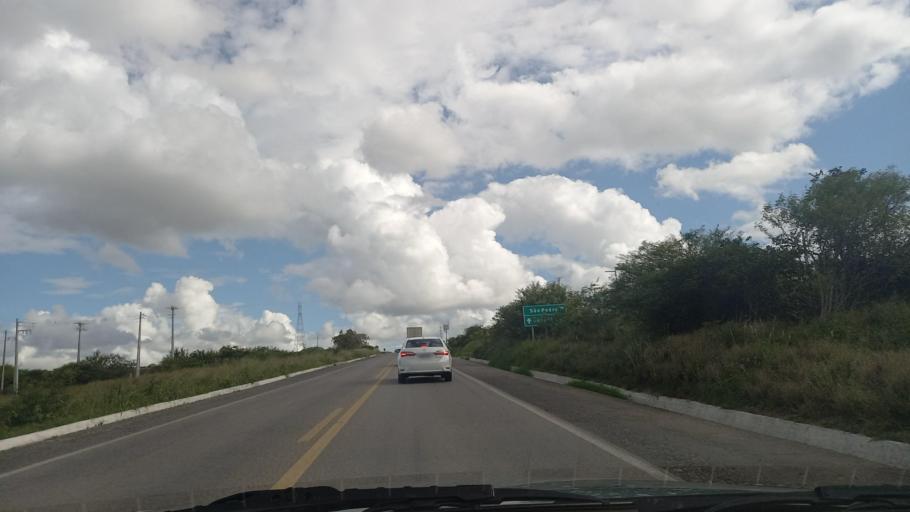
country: BR
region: Pernambuco
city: Garanhuns
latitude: -8.8298
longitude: -36.4525
